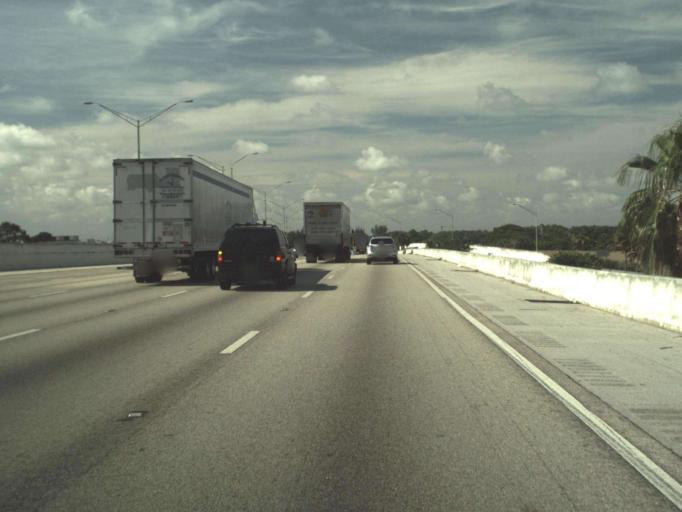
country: US
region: Florida
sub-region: Palm Beach County
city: Mangonia Park
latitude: 26.7828
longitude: -80.0994
